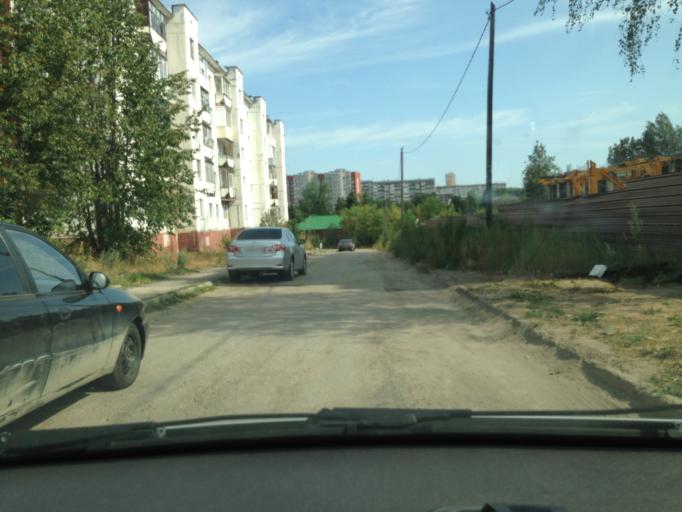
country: RU
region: Udmurtiya
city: Izhevsk
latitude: 56.8734
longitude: 53.1943
